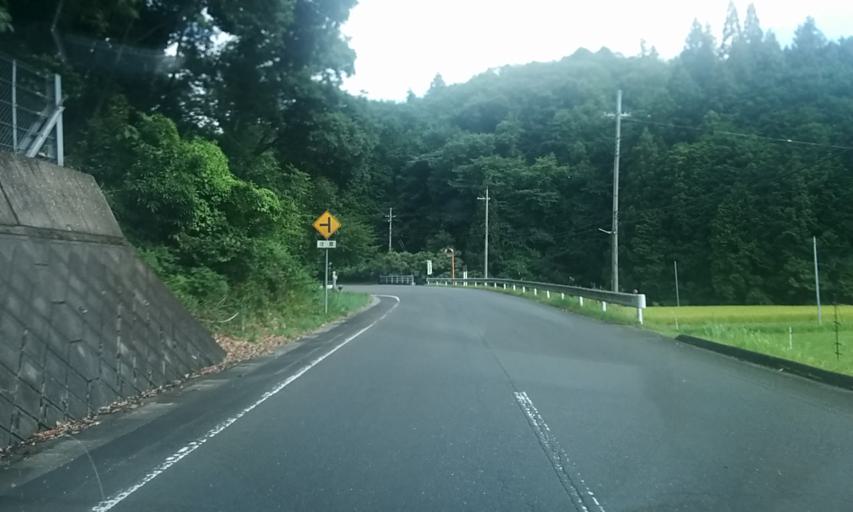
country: JP
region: Kyoto
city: Fukuchiyama
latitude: 35.3585
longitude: 135.1406
